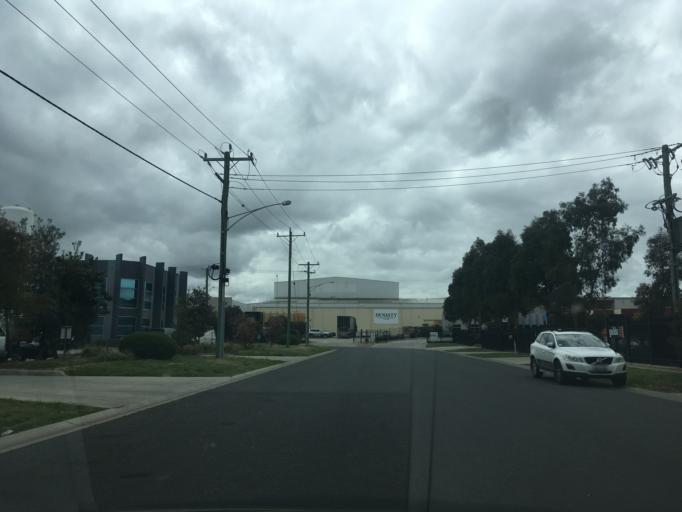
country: AU
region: Victoria
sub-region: Brimbank
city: Sunshine West
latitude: -37.8214
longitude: 144.8016
